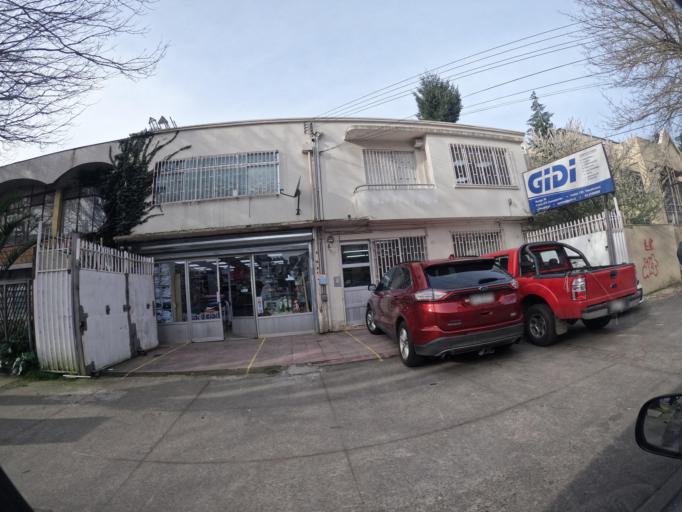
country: CL
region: Biobio
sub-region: Provincia de Concepcion
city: Concepcion
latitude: -36.8323
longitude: -73.0492
